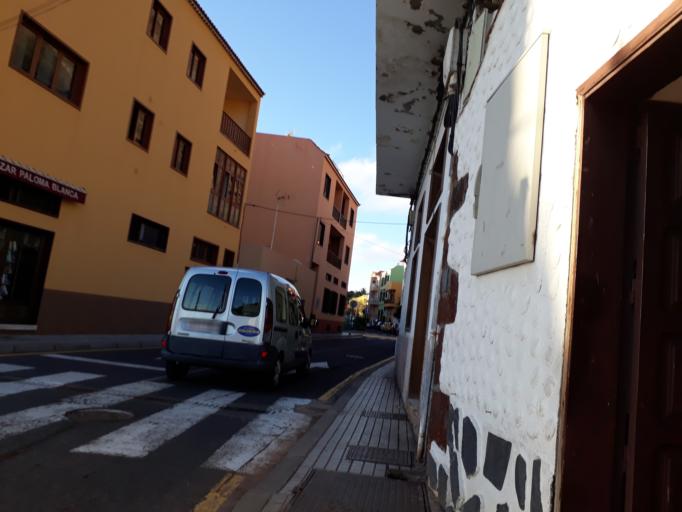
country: ES
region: Canary Islands
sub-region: Provincia de Santa Cruz de Tenerife
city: Alajero
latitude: 28.0955
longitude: -17.3422
